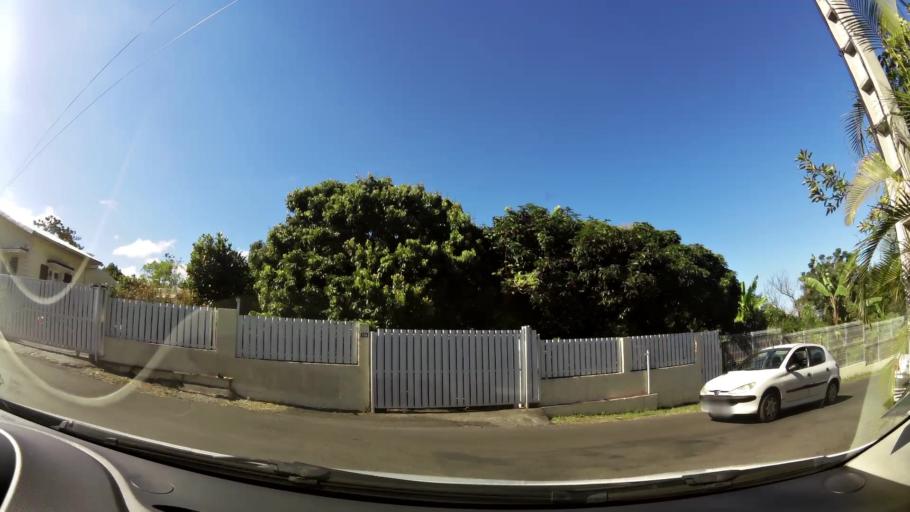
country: RE
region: Reunion
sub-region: Reunion
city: Le Tampon
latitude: -21.2630
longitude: 55.5034
